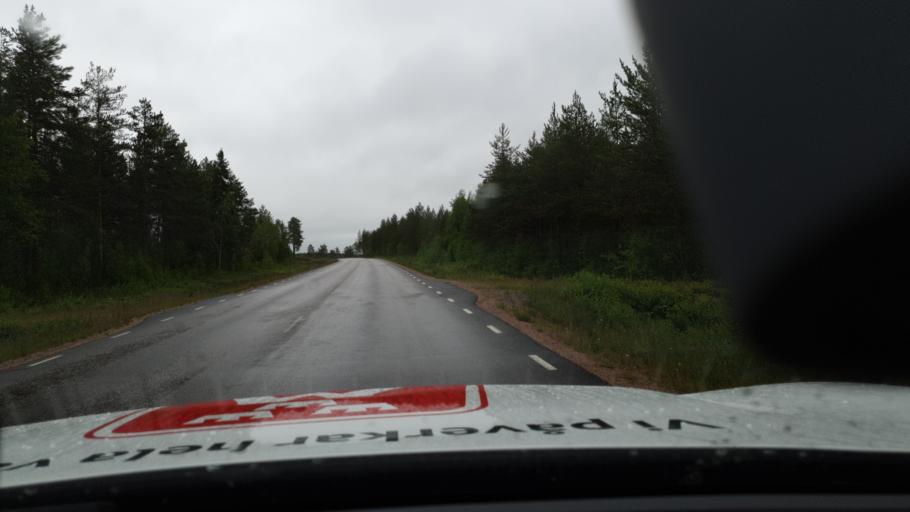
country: SE
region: Norrbotten
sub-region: Overtornea Kommun
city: OEvertornea
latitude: 66.4848
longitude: 23.7033
